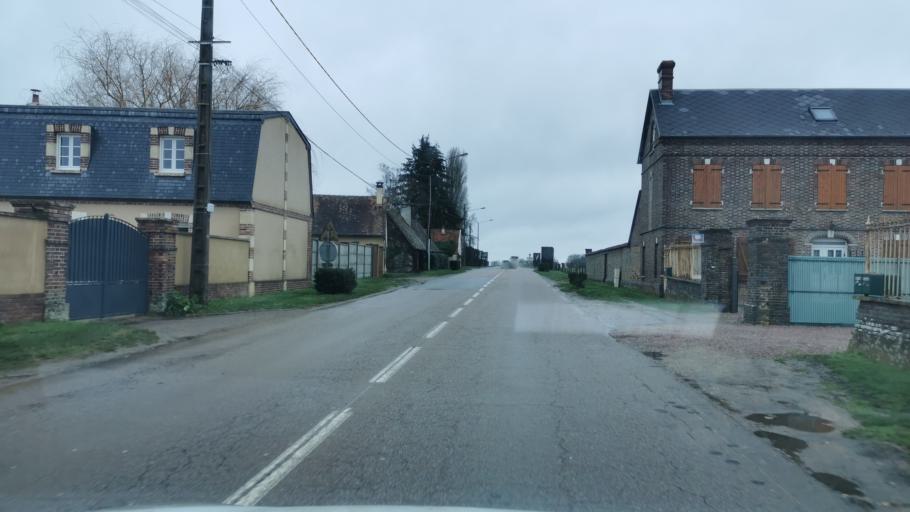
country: FR
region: Haute-Normandie
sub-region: Departement de l'Eure
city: Normanville
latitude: 49.0846
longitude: 1.1804
